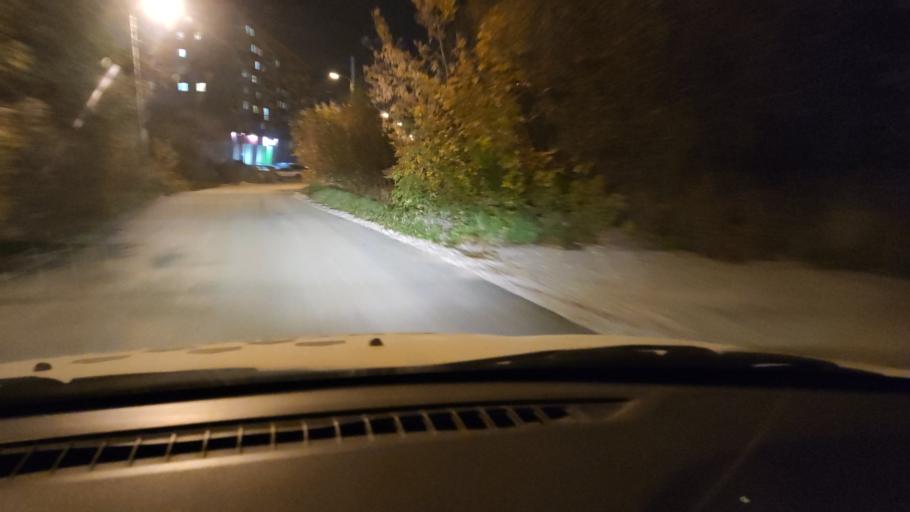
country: RU
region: Perm
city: Perm
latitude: 57.9774
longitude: 56.2982
